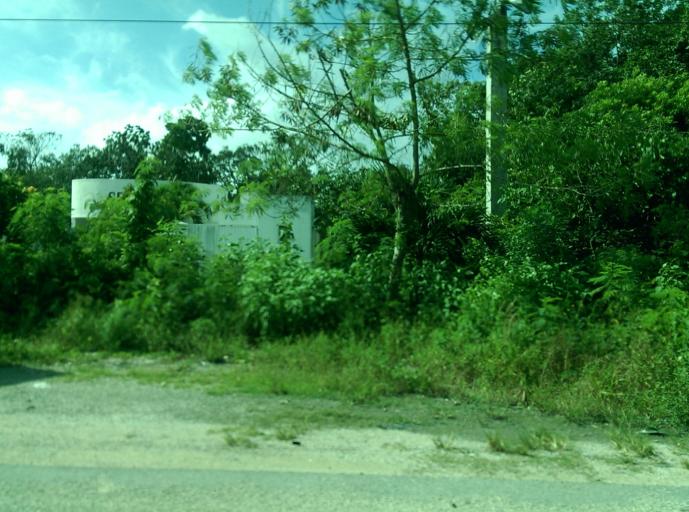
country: MX
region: Quintana Roo
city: Tulum
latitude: 20.2279
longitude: -87.4583
